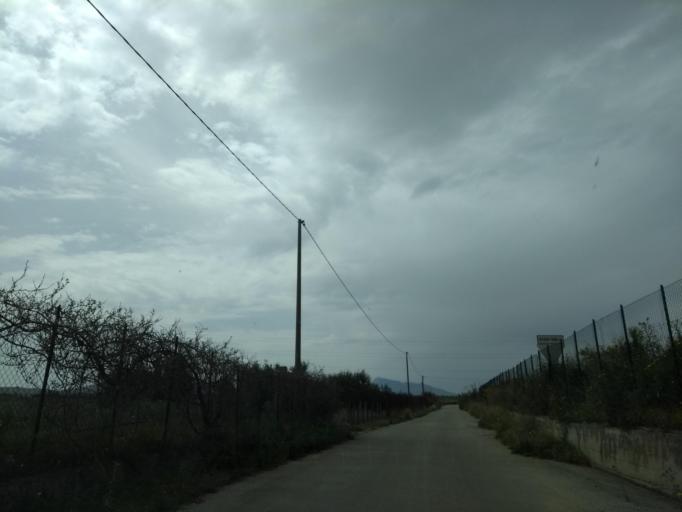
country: IT
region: Sicily
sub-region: Palermo
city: Partinico
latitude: 37.9907
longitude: 13.0698
